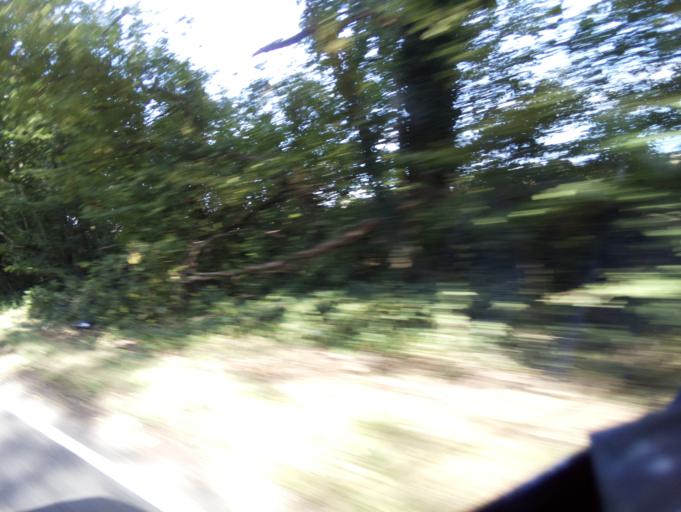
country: GB
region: England
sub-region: Hampshire
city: Four Marks
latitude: 51.0580
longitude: -1.0346
